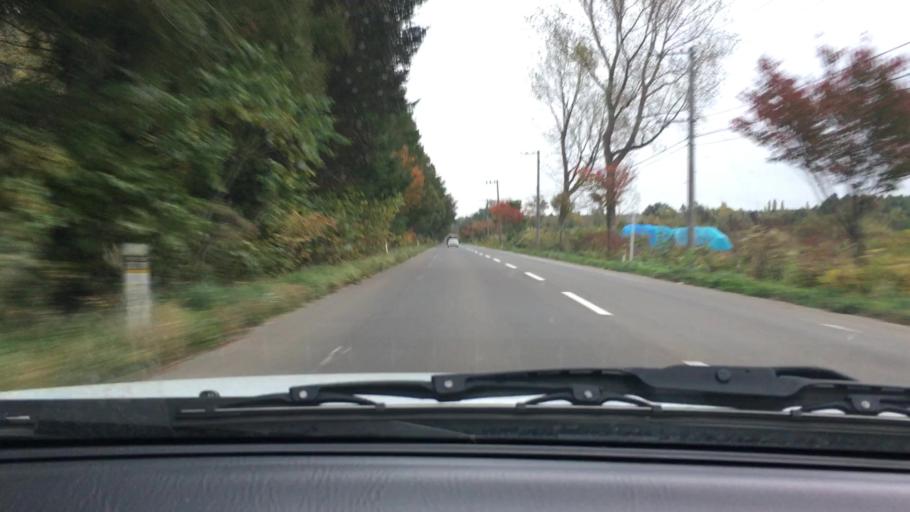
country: JP
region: Aomori
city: Shimokizukuri
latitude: 40.7166
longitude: 140.3126
